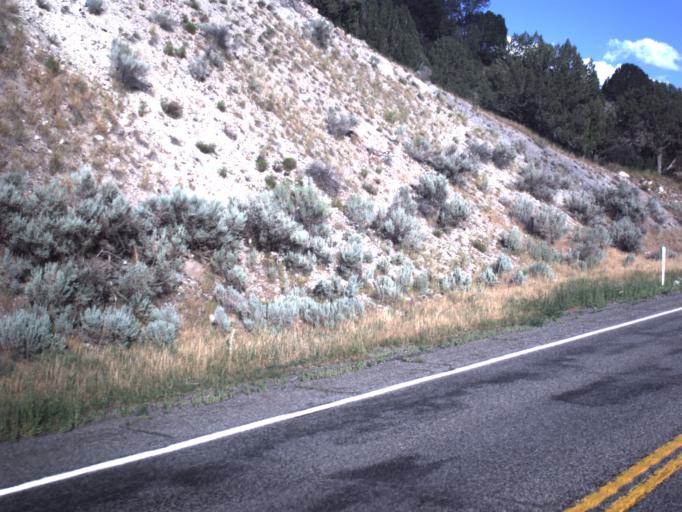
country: US
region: Utah
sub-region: Utah County
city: Woodland Hills
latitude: 39.8801
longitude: -111.5434
